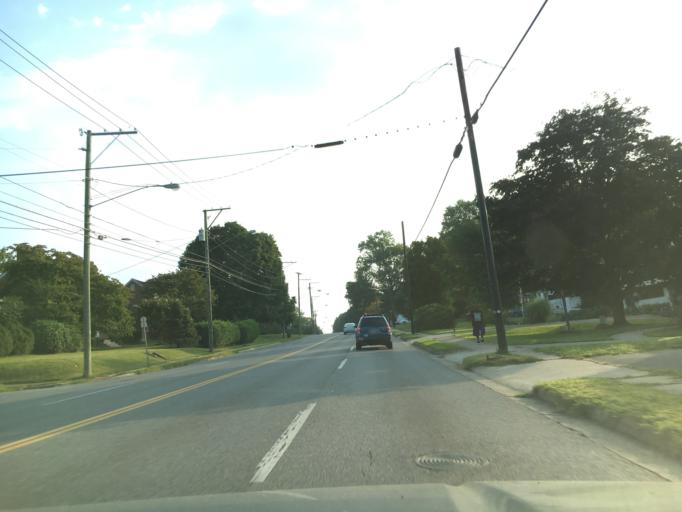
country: US
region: Virginia
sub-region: City of Lynchburg
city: West Lynchburg
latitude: 37.3857
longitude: -79.1770
